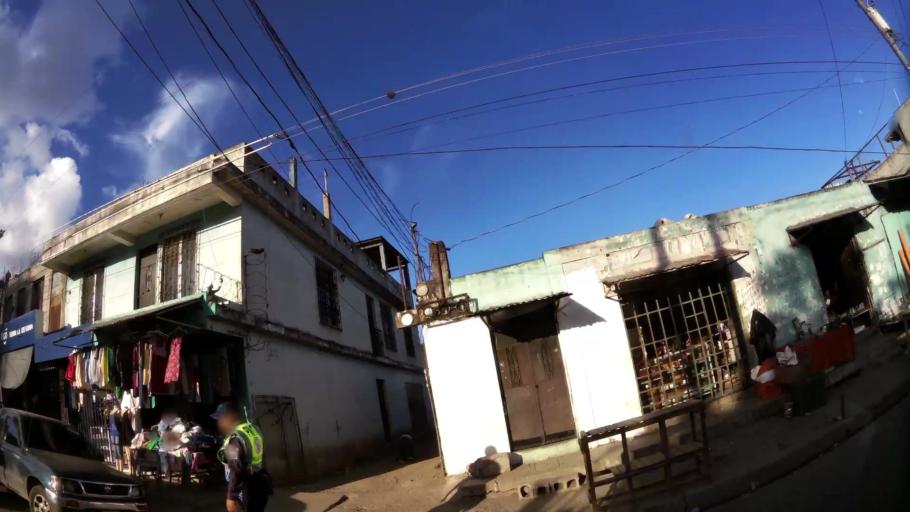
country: GT
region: Guatemala
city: Villa Nueva
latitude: 14.5220
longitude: -90.5882
